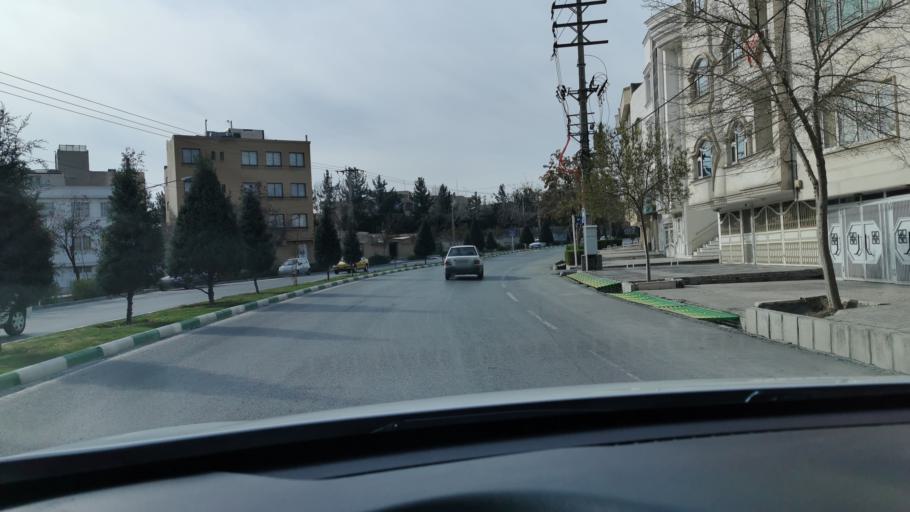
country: IR
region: Razavi Khorasan
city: Mashhad
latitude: 36.3116
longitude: 59.5159
